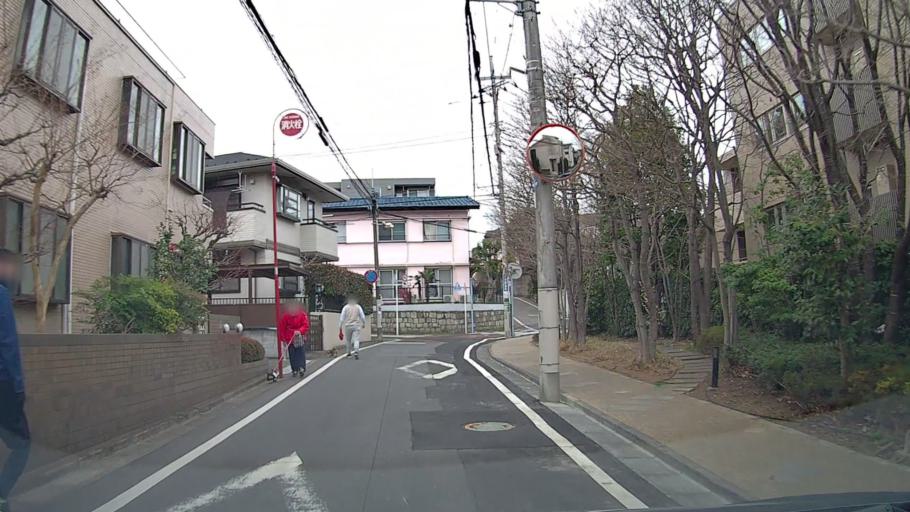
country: JP
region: Tokyo
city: Tokyo
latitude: 35.6897
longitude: 139.6439
